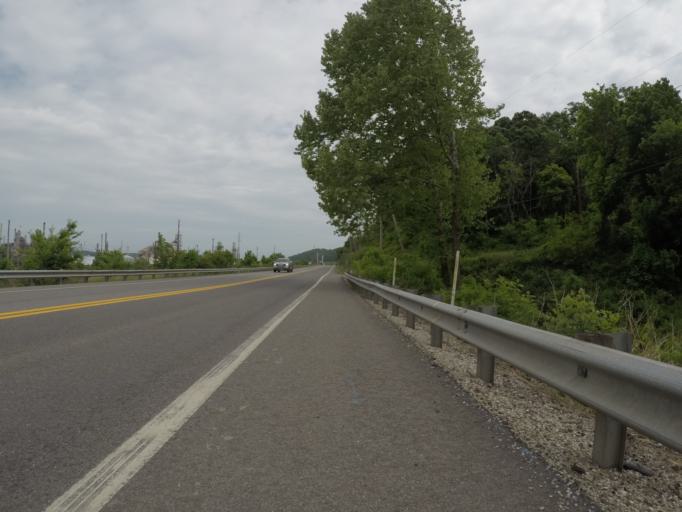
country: US
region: West Virginia
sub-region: Wayne County
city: Kenova
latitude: 38.3654
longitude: -82.5927
